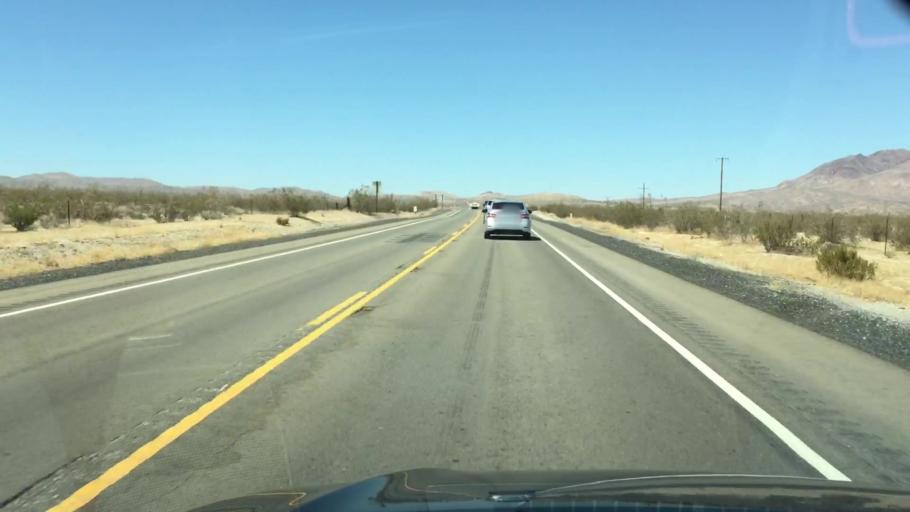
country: US
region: California
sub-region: Kern County
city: Boron
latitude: 35.2732
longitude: -117.6146
